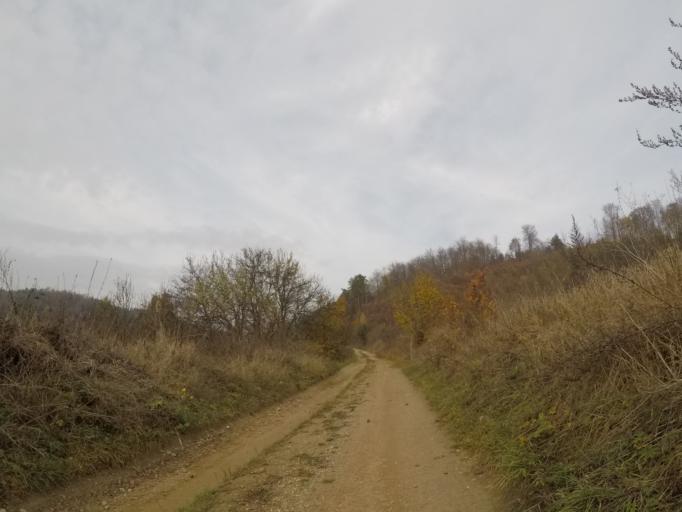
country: SK
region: Presovsky
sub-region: Okres Presov
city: Presov
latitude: 48.9192
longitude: 21.1434
